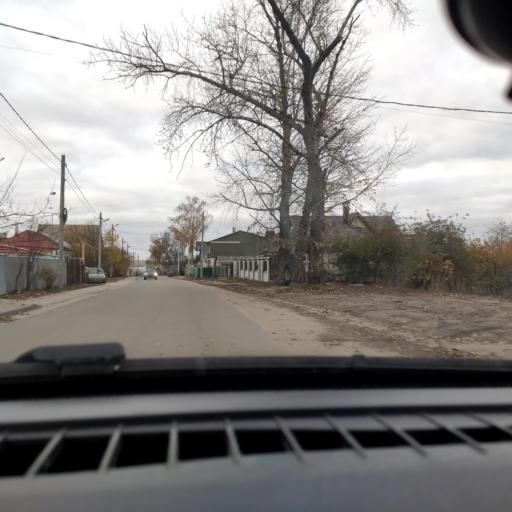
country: RU
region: Voronezj
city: Podgornoye
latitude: 51.7313
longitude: 39.1593
